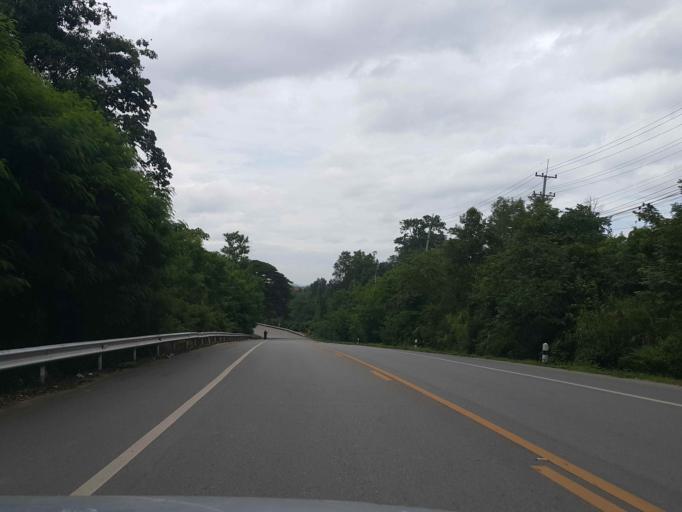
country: TH
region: Lamphun
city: Li
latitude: 17.7848
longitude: 98.9537
